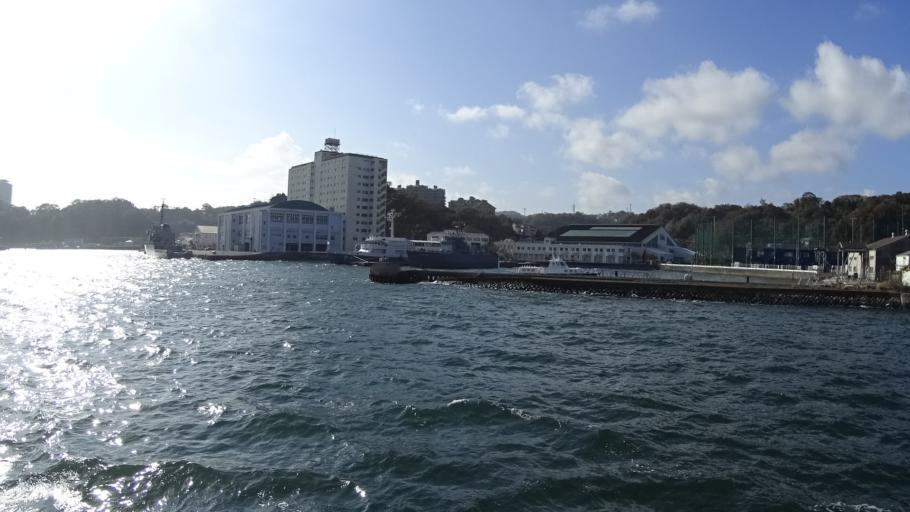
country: JP
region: Kanagawa
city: Yokosuka
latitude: 35.2932
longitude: 139.6491
